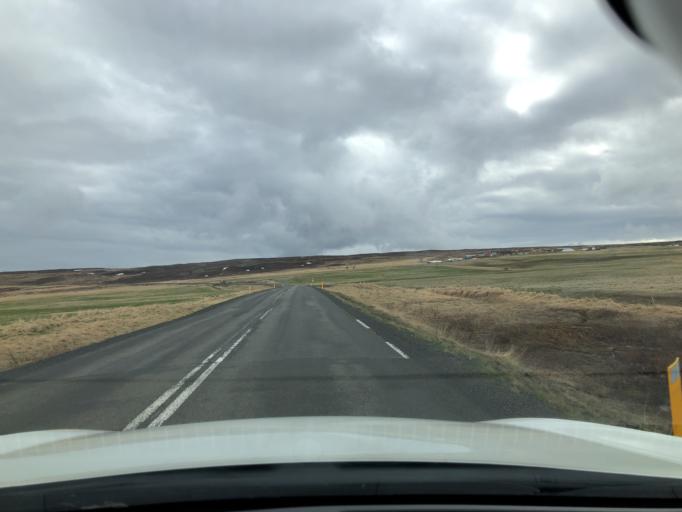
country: IS
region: Northeast
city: Laugar
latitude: 65.6865
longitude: -17.5315
